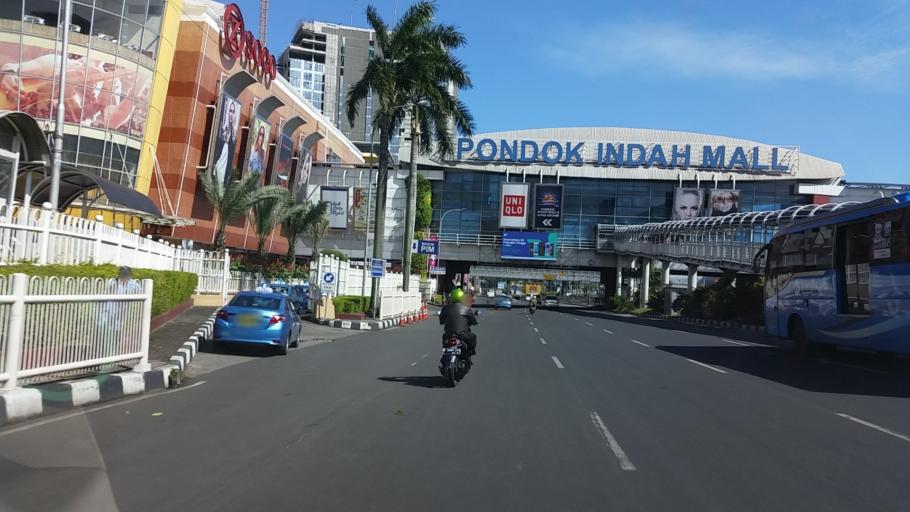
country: ID
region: Banten
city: South Tangerang
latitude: -6.2673
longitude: 106.7836
